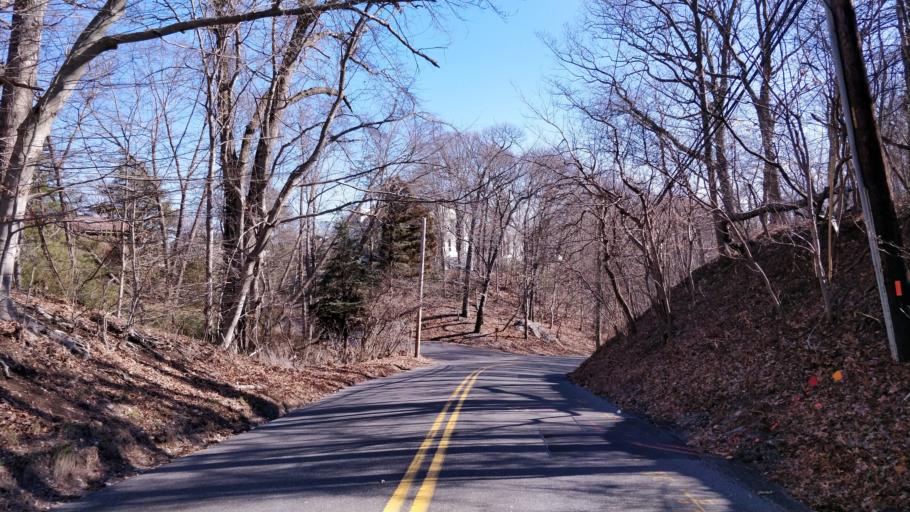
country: US
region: New York
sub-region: Suffolk County
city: Mount Sinai
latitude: 40.9479
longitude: -73.0465
